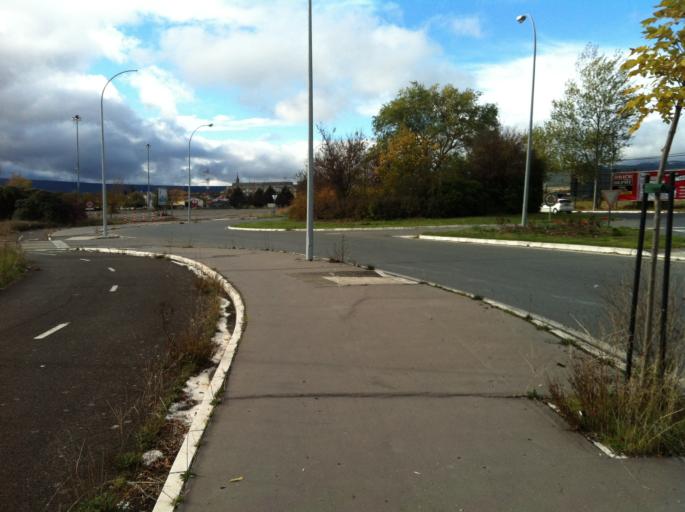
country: ES
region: Basque Country
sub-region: Provincia de Alava
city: Gasteiz / Vitoria
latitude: 42.8597
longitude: -2.7256
